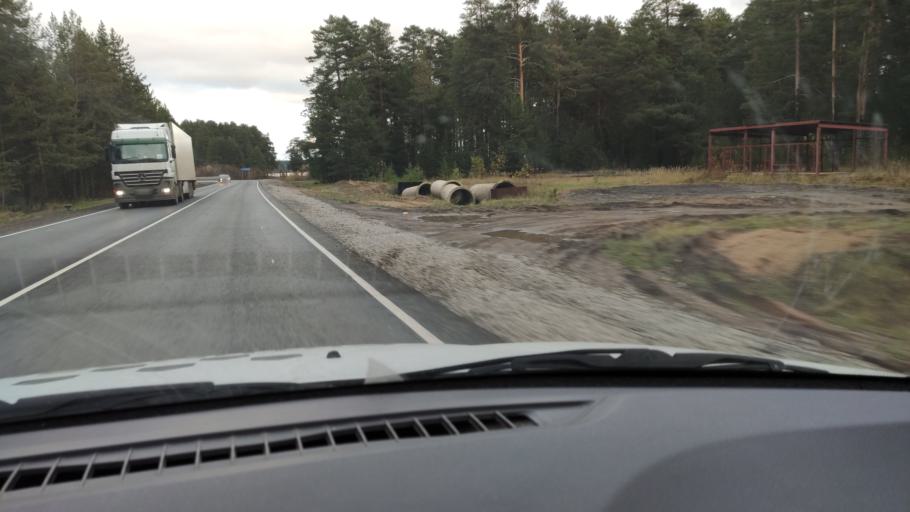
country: RU
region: Kirov
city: Belaya Kholunitsa
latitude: 58.8579
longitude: 50.8407
